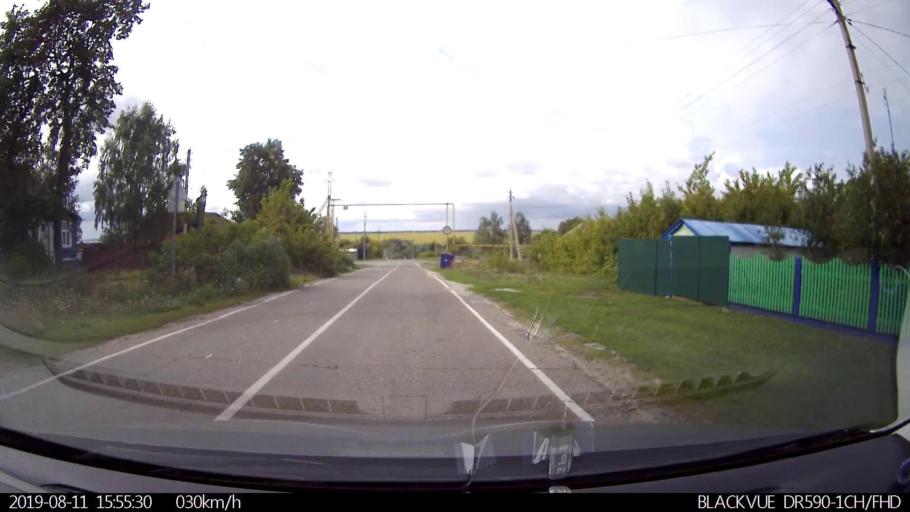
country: RU
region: Ulyanovsk
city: Ignatovka
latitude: 53.9454
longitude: 47.6539
